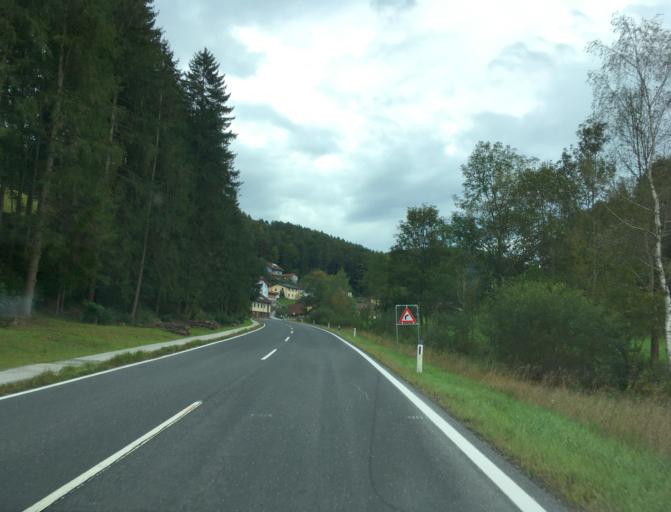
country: AT
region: Lower Austria
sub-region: Politischer Bezirk Neunkirchen
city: Edlitz
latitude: 47.5901
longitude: 16.1459
